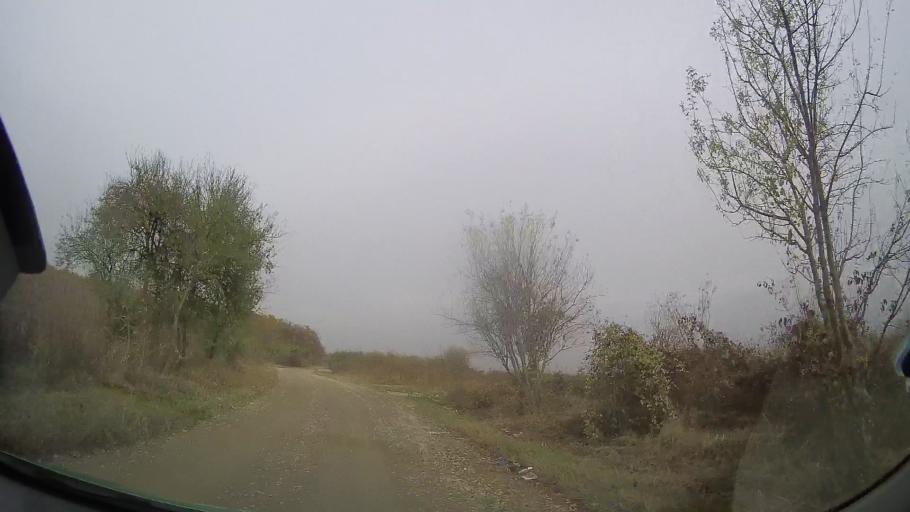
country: RO
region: Prahova
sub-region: Comuna Gorgota
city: Potigrafu
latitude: 44.7498
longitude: 26.1226
